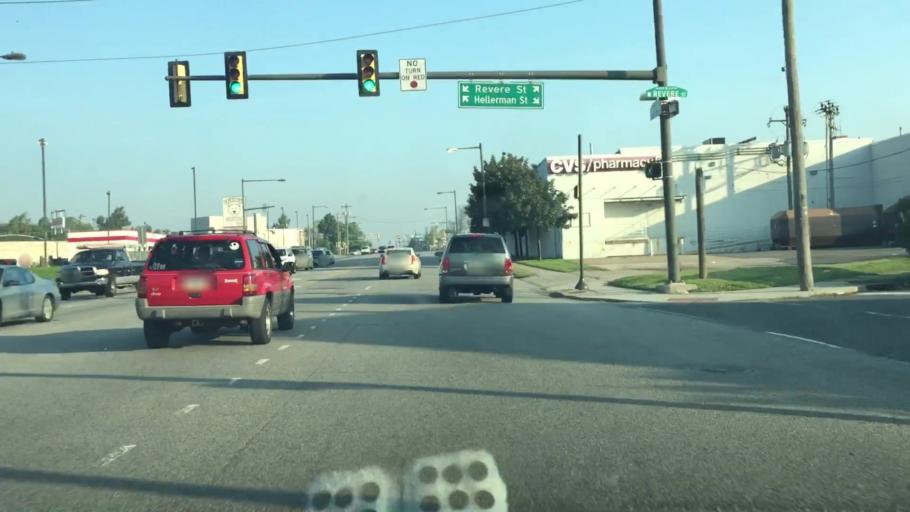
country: US
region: New Jersey
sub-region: Burlington County
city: Palmyra
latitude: 40.0337
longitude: -75.0636
